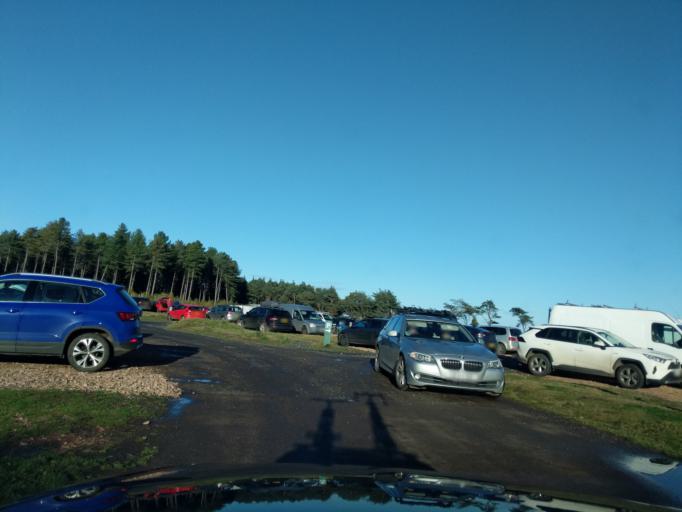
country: GB
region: Scotland
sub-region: Fife
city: Saint Andrews
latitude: 56.4080
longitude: -2.8143
